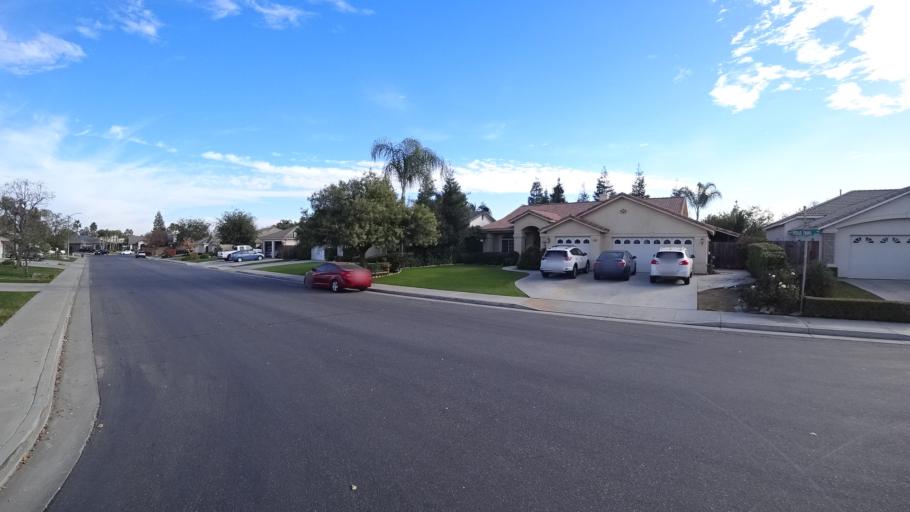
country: US
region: California
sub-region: Kern County
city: Greenacres
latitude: 35.4047
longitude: -119.1145
